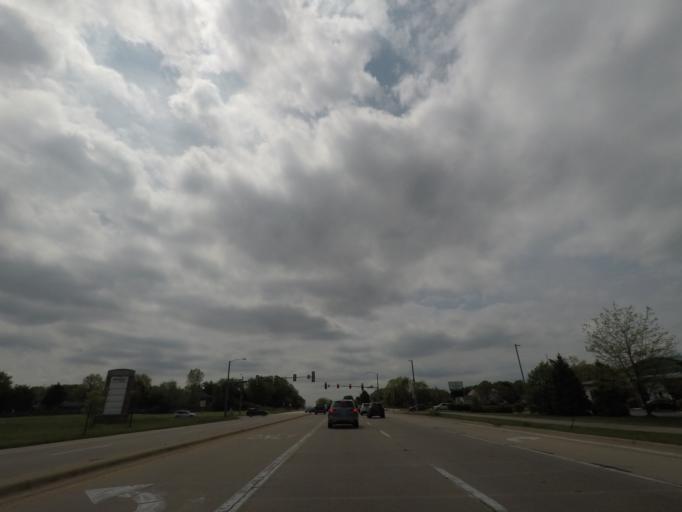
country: US
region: Illinois
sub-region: Winnebago County
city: Cherry Valley
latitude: 42.2913
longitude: -88.9803
